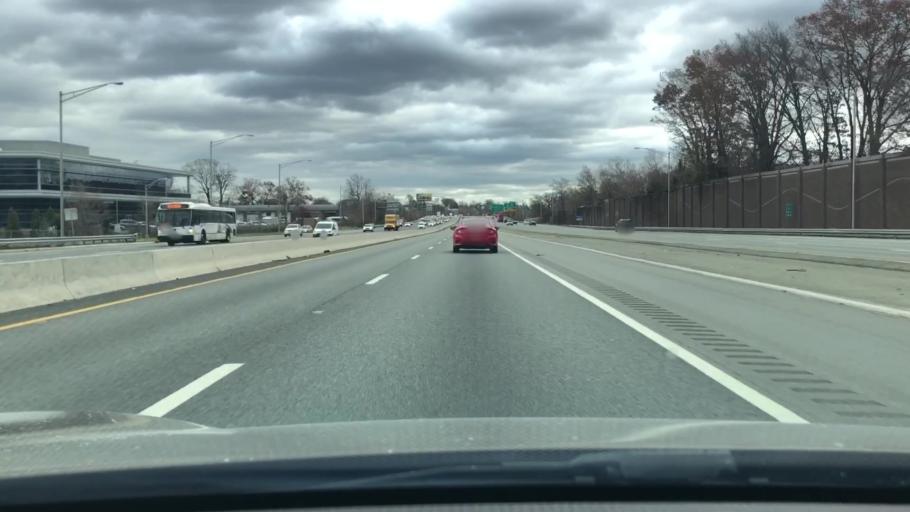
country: US
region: New Jersey
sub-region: Bergen County
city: Lodi
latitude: 40.8914
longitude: -74.0743
